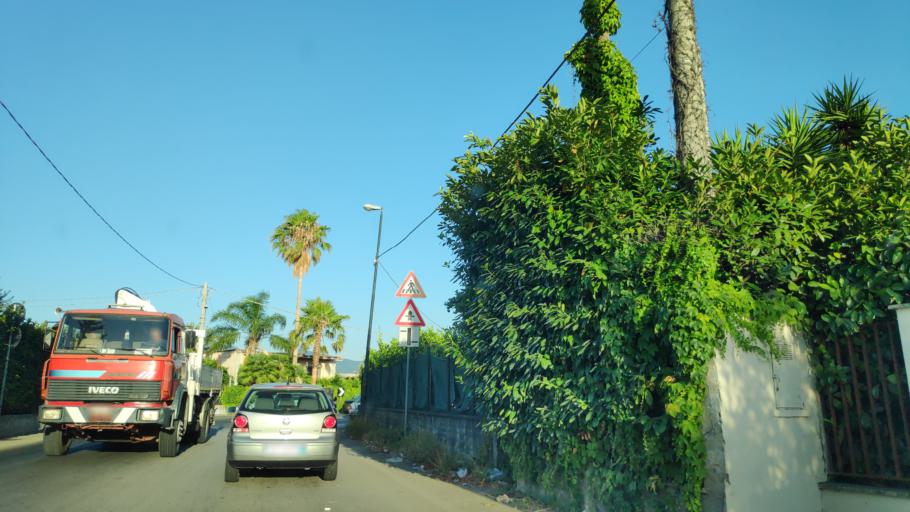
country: IT
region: Campania
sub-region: Provincia di Salerno
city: Pagani
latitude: 40.7628
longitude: 14.6148
